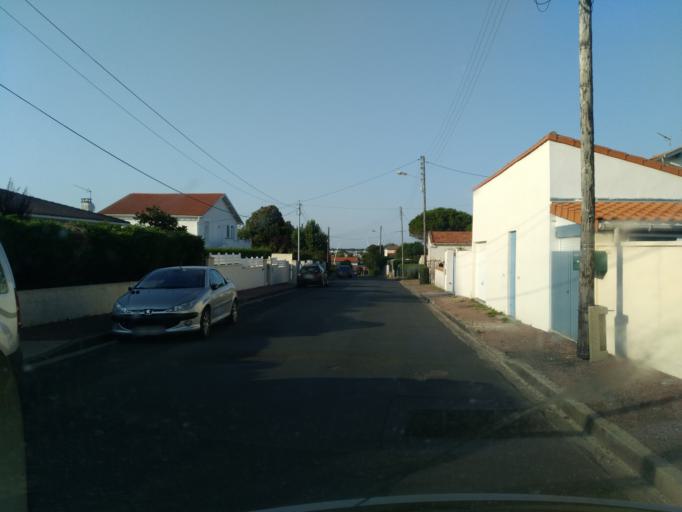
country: FR
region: Poitou-Charentes
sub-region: Departement de la Charente-Maritime
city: Vaux-sur-Mer
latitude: 45.6357
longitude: -1.0608
